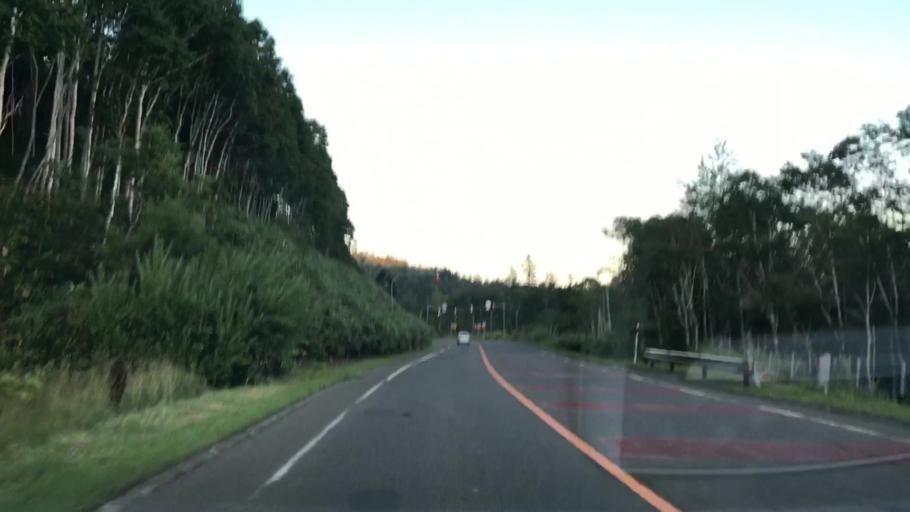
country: JP
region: Hokkaido
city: Sapporo
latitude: 42.8717
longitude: 141.1168
